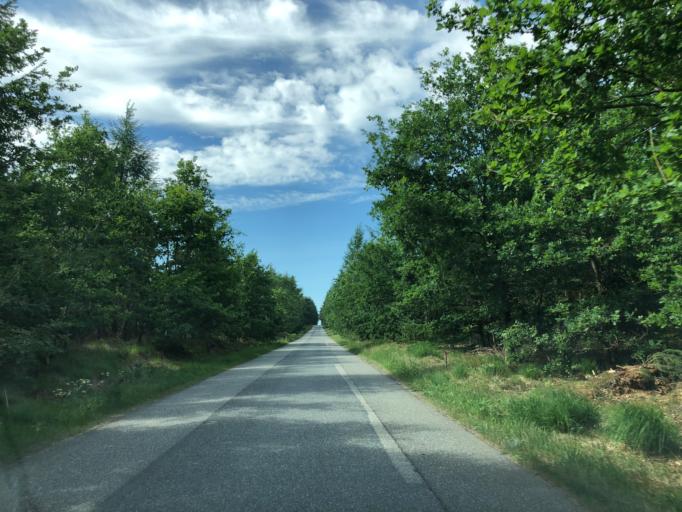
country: DK
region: Central Jutland
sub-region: Herning Kommune
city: Lind
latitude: 56.0391
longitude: 8.9371
